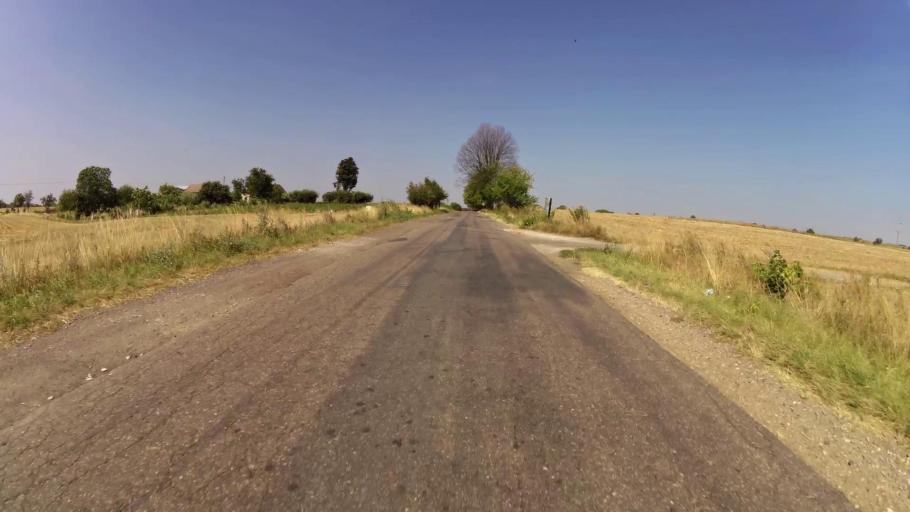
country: PL
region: West Pomeranian Voivodeship
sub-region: Powiat walecki
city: Walcz
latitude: 53.2230
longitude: 16.4677
